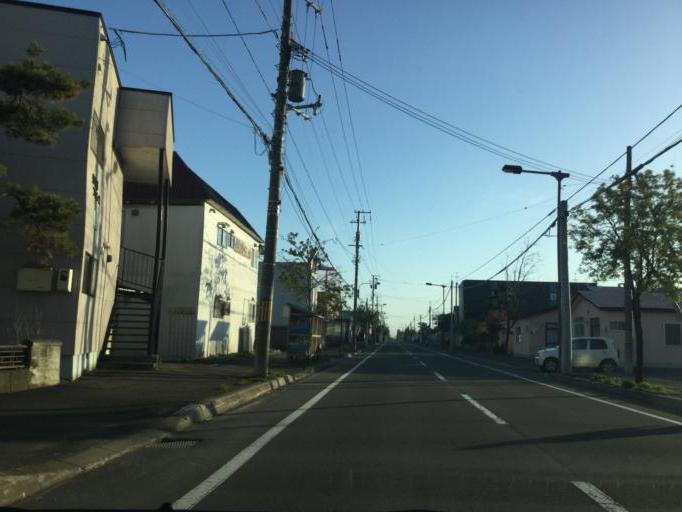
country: JP
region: Hokkaido
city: Iwamizawa
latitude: 43.2092
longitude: 141.7739
